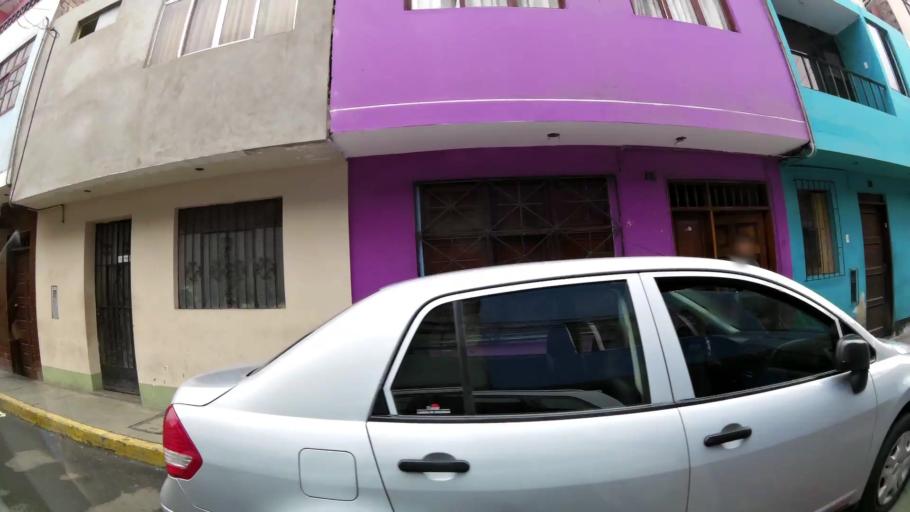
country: PE
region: Lima
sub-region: Lima
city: Surco
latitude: -12.1154
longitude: -77.0153
